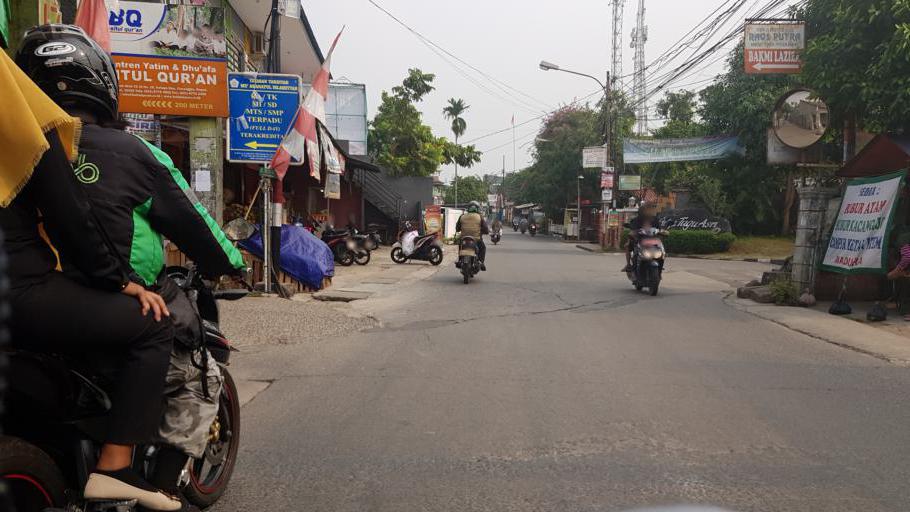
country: ID
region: West Java
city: Depok
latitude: -6.3630
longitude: 106.8431
